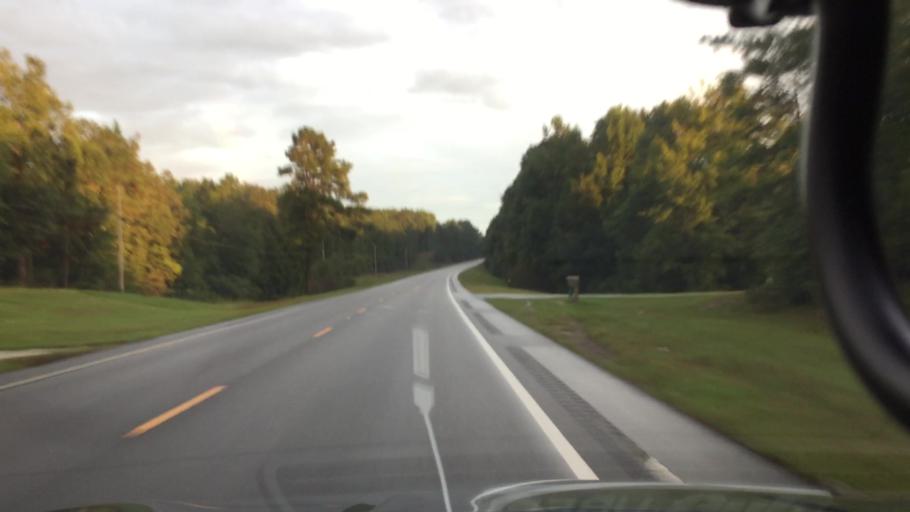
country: US
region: Alabama
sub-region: Coffee County
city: New Brockton
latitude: 31.5549
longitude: -85.9214
